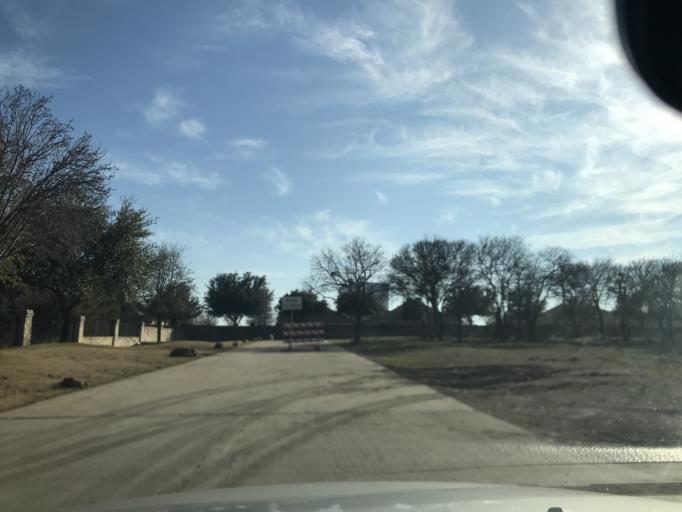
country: US
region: Texas
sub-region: Denton County
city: The Colony
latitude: 33.0917
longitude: -96.8363
